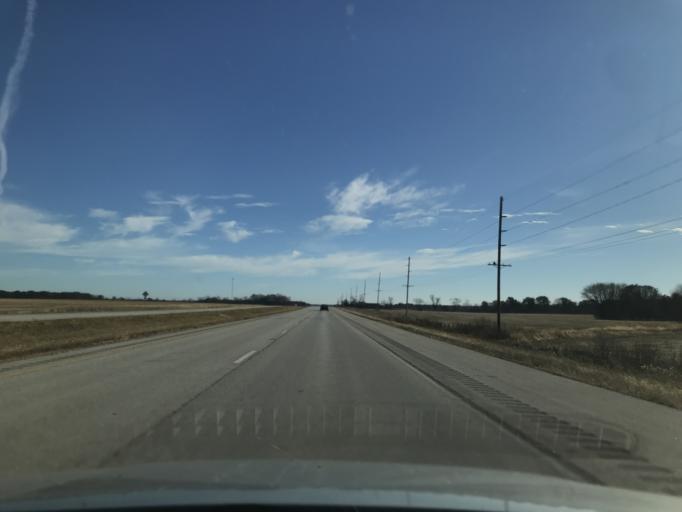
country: US
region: Illinois
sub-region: Hancock County
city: Carthage
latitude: 40.4149
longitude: -91.0514
